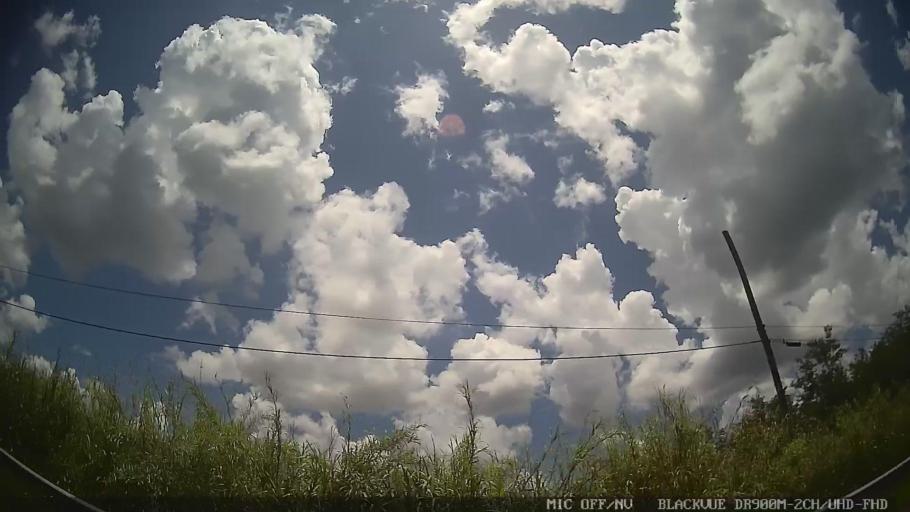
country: BR
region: Sao Paulo
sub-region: Amparo
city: Amparo
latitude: -22.6657
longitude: -46.7414
